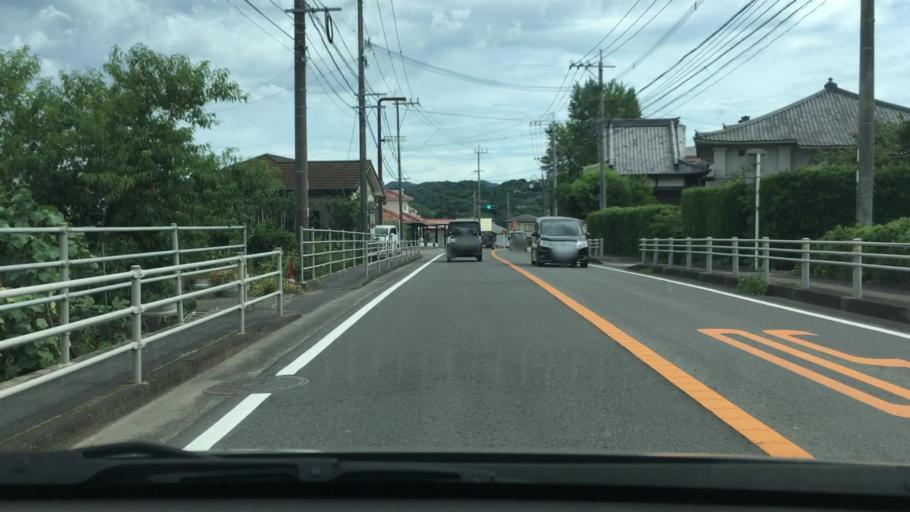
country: JP
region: Nagasaki
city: Togitsu
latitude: 32.9005
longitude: 129.7807
